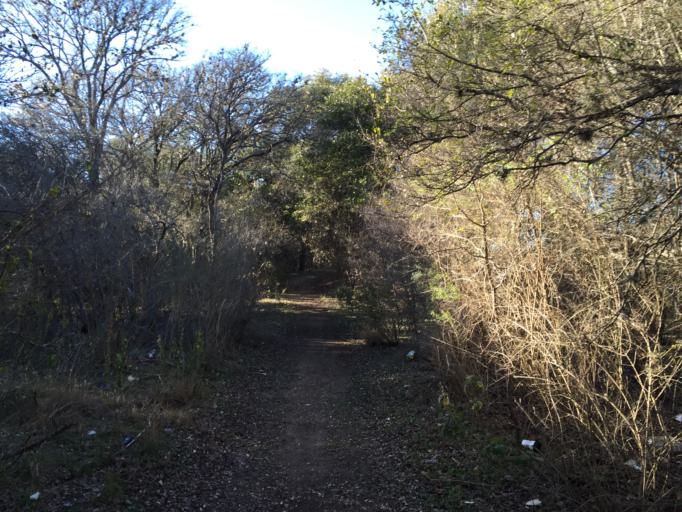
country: US
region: Texas
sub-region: Bexar County
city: Castle Hills
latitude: 29.5591
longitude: -98.5025
